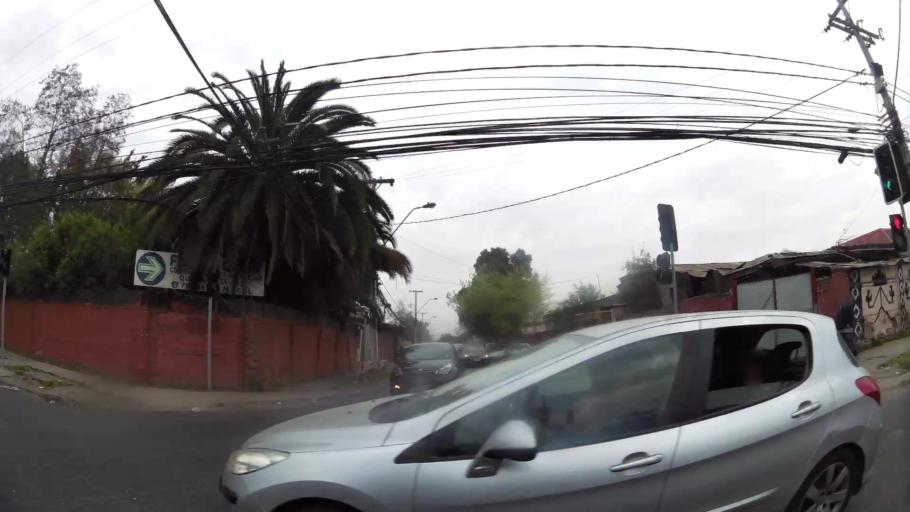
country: CL
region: Santiago Metropolitan
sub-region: Provincia de Santiago
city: Villa Presidente Frei, Nunoa, Santiago, Chile
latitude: -33.4848
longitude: -70.6017
